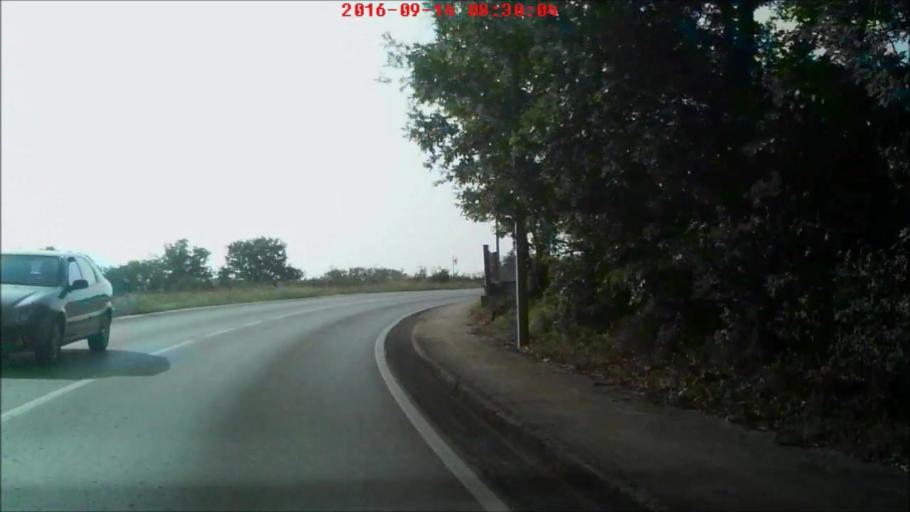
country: HR
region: Zadarska
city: Zadar
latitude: 44.1758
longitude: 15.2887
